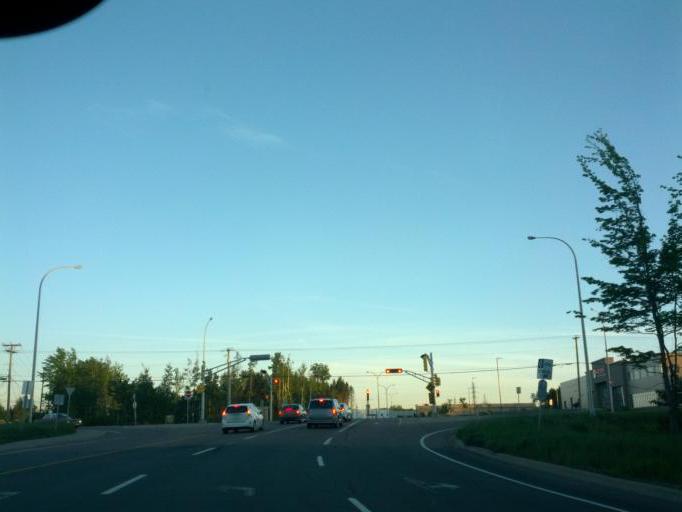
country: CA
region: New Brunswick
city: Moncton
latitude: 46.0984
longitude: -64.8602
